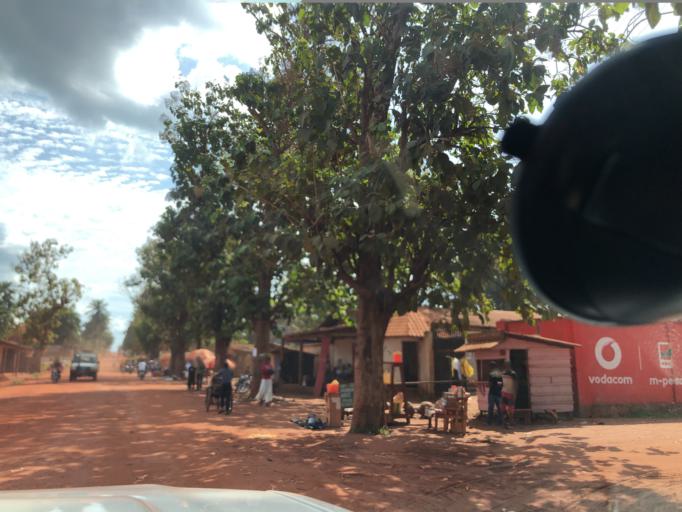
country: CD
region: Equateur
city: Gemena
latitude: 3.2450
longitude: 19.7820
